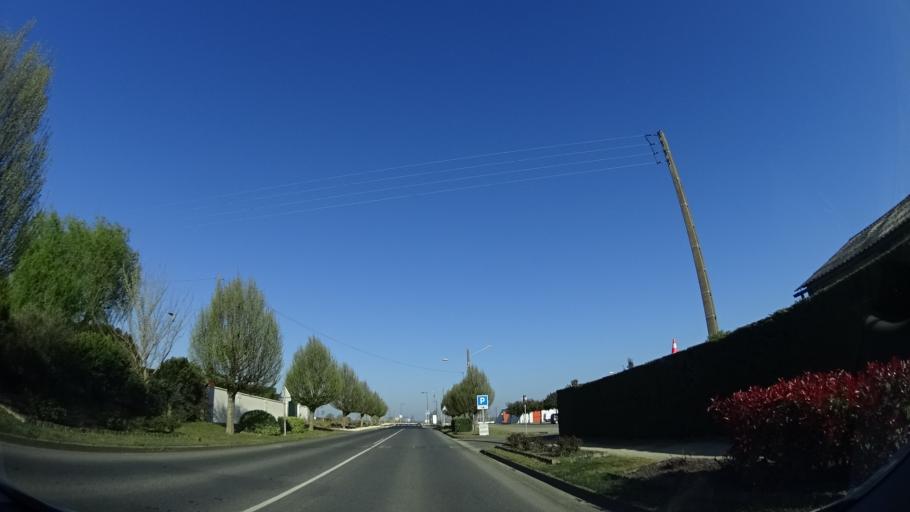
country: FR
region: Pays de la Loire
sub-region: Departement de Maine-et-Loire
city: Doue-la-Fontaine
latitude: 47.2009
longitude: -0.2819
